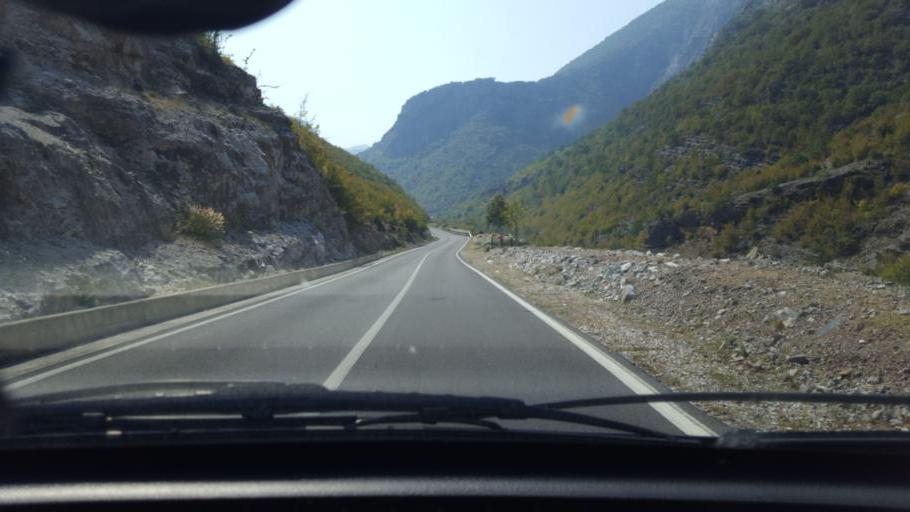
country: AL
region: Shkoder
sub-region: Rrethi i Malesia e Madhe
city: Kastrat
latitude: 42.4494
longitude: 19.5481
